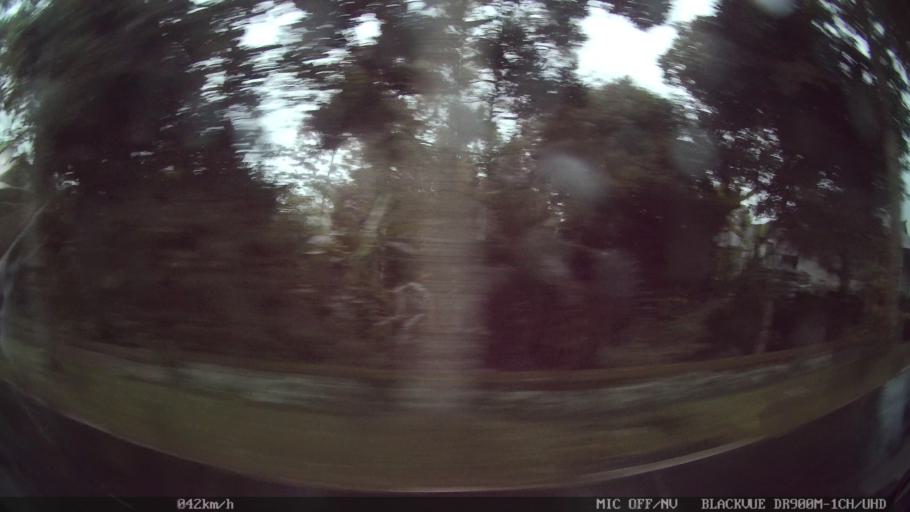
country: ID
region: Bali
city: Banjar Taro Kelod
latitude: -8.3255
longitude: 115.2938
